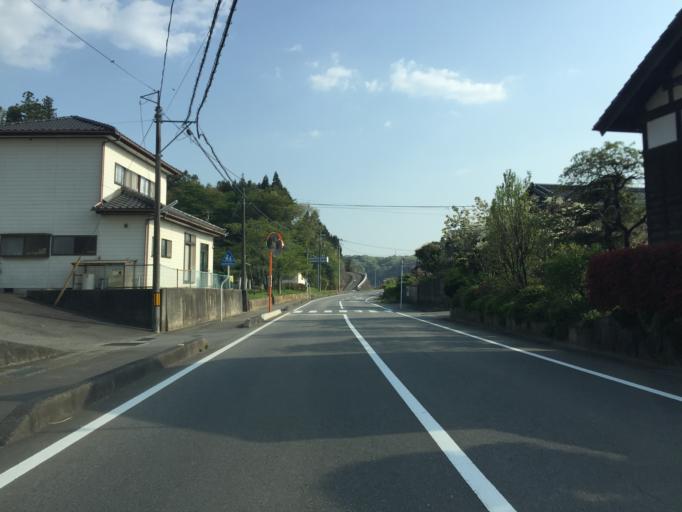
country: JP
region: Fukushima
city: Iwaki
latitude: 36.9789
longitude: 140.8010
